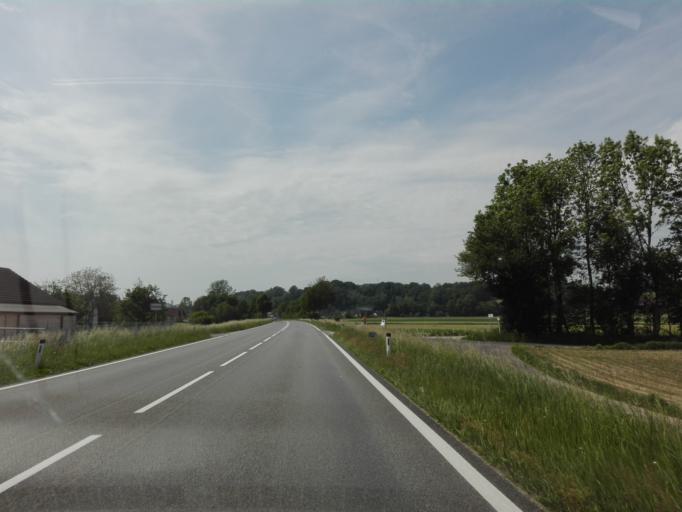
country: AT
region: Upper Austria
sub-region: Politischer Bezirk Perg
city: Bad Kreuzen
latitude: 48.2200
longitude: 14.7345
